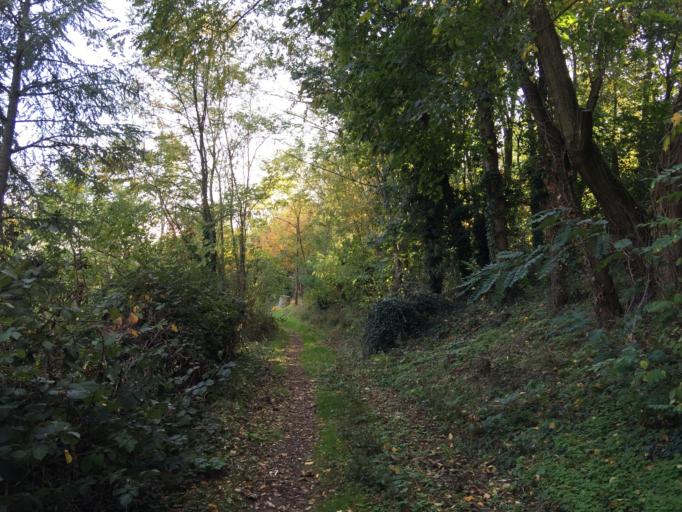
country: FR
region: Rhone-Alpes
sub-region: Departement de la Loire
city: Saint-Etienne
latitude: 45.4485
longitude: 4.3769
